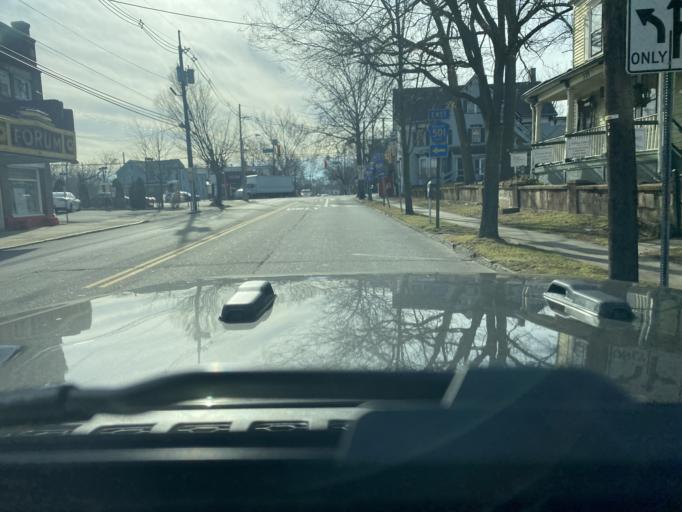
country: US
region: New Jersey
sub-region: Middlesex County
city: Metuchen
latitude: 40.5386
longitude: -74.3604
